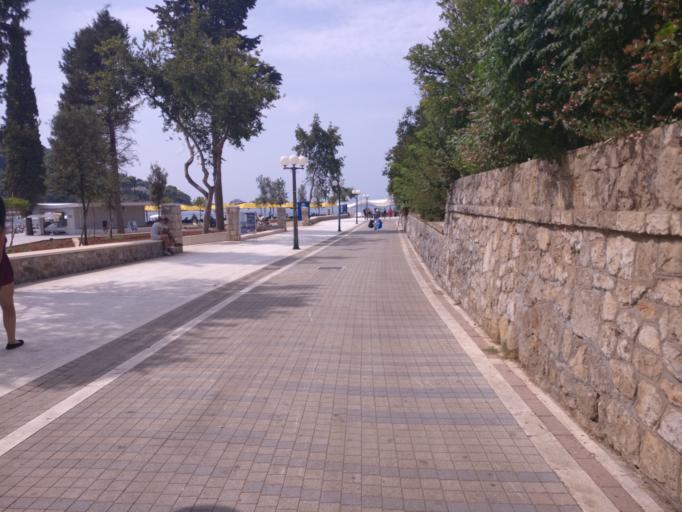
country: HR
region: Dubrovacko-Neretvanska
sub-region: Grad Dubrovnik
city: Dubrovnik
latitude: 42.6558
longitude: 18.0712
